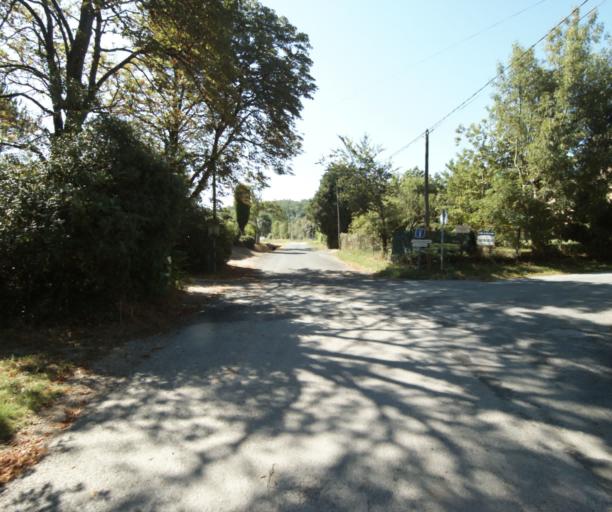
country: FR
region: Midi-Pyrenees
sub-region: Departement de la Haute-Garonne
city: Revel
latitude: 43.4508
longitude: 2.0187
